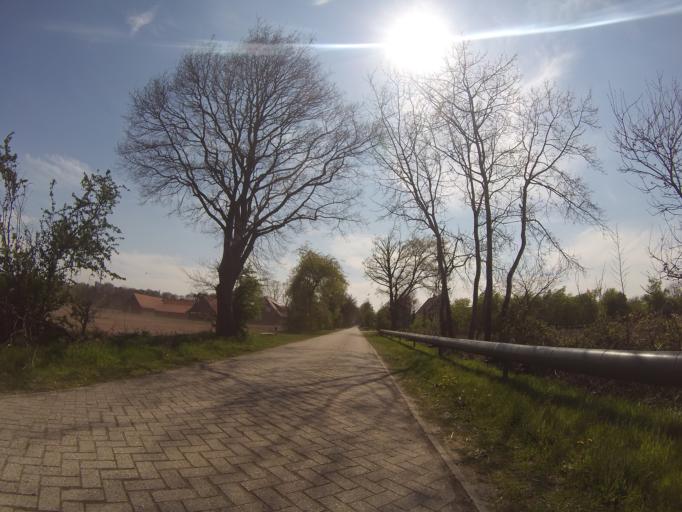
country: DE
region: Lower Saxony
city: Emlichheim
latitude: 52.6246
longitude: 6.8692
